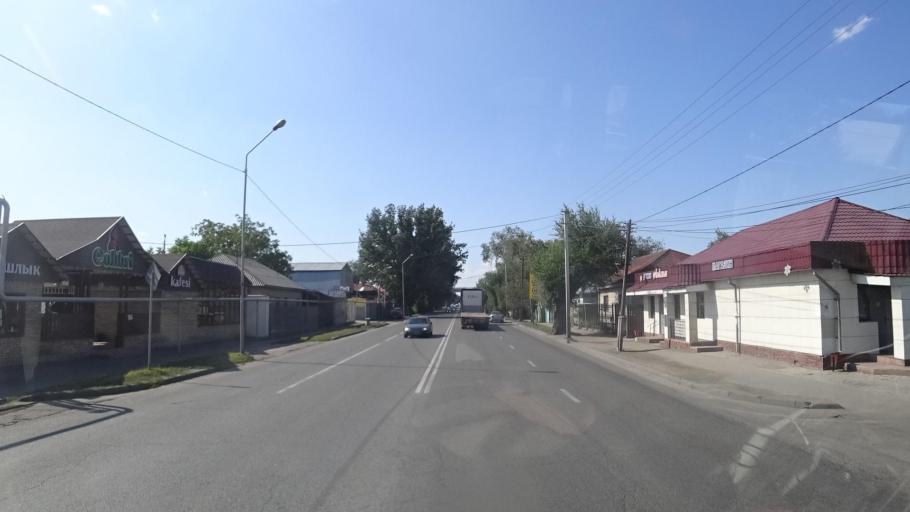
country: KZ
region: Almaty Oblysy
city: Pervomayskiy
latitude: 43.3529
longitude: 76.9548
